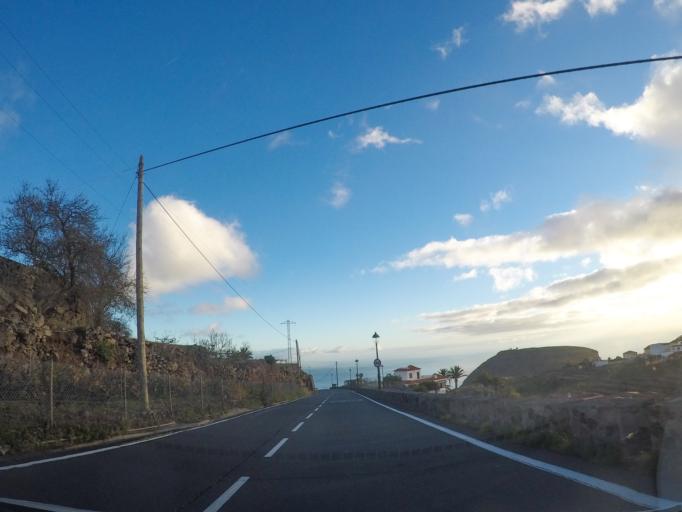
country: ES
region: Canary Islands
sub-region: Provincia de Santa Cruz de Tenerife
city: Alajero
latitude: 28.0629
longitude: -17.2371
